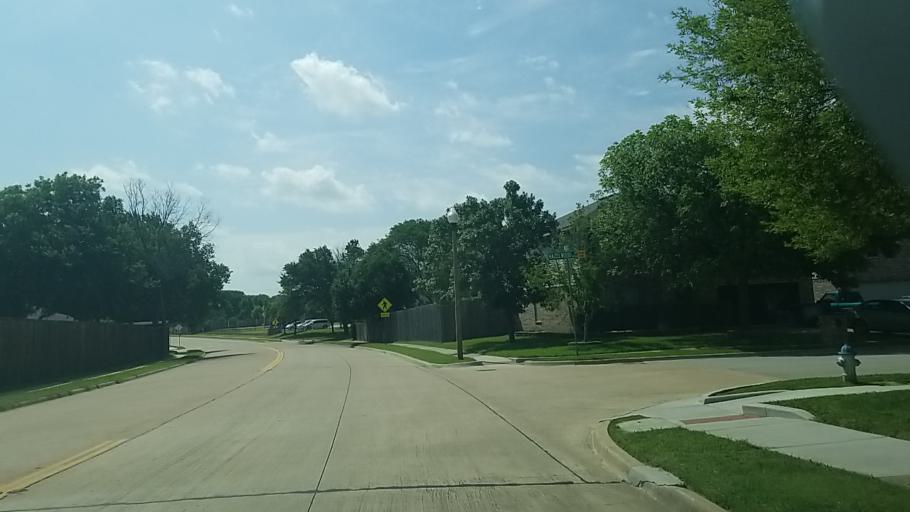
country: US
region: Texas
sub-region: Denton County
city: Copper Canyon
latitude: 33.1430
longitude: -97.1191
